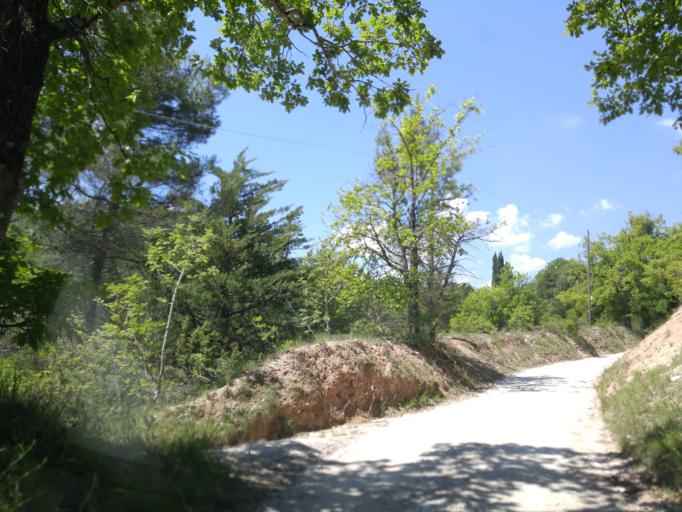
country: IT
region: The Marches
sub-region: Provincia di Pesaro e Urbino
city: Canavaccio
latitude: 43.7148
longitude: 12.6897
